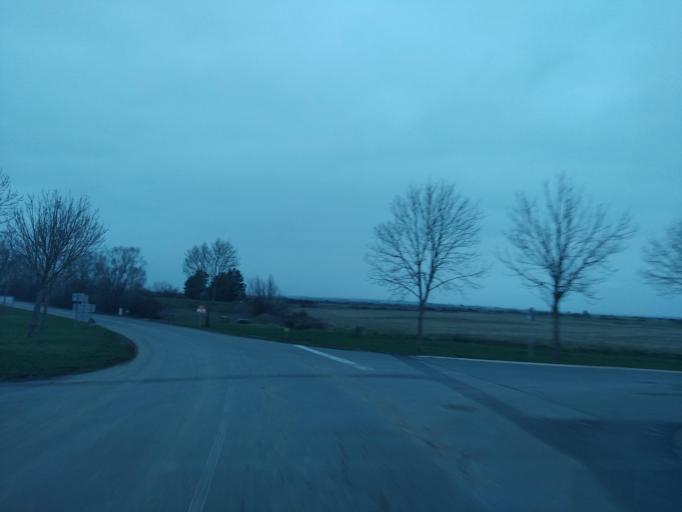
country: FR
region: Pays de la Loire
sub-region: Departement de la Vendee
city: Triaize
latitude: 46.3613
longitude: -1.2492
